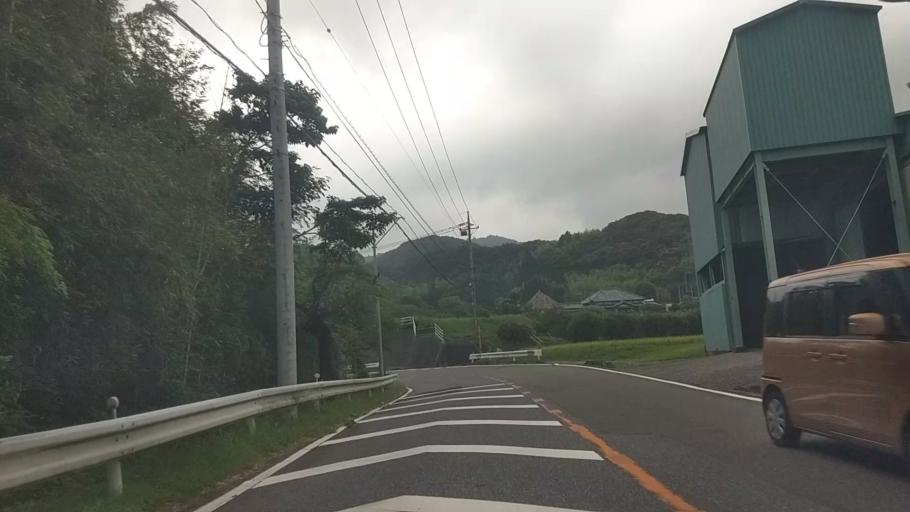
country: JP
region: Chiba
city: Kawaguchi
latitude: 35.1397
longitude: 139.9775
